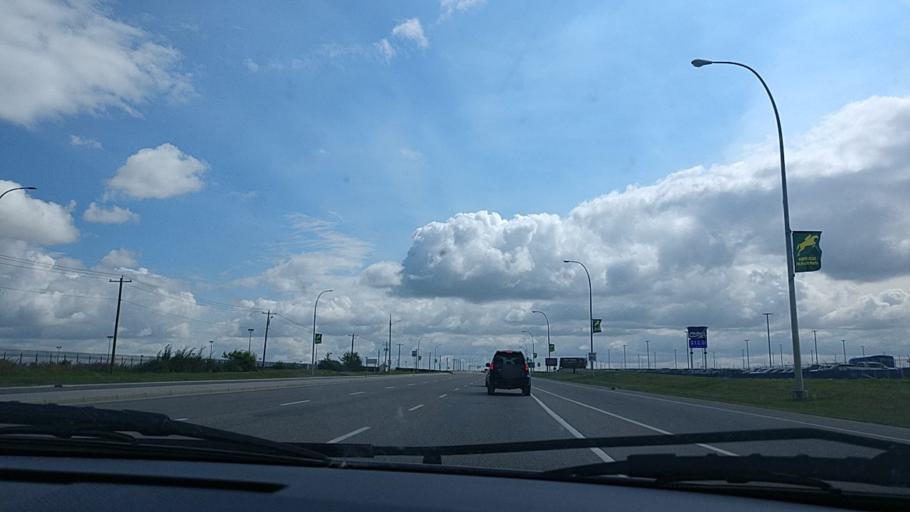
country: CA
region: Alberta
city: Calgary
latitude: 51.1394
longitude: -114.0119
